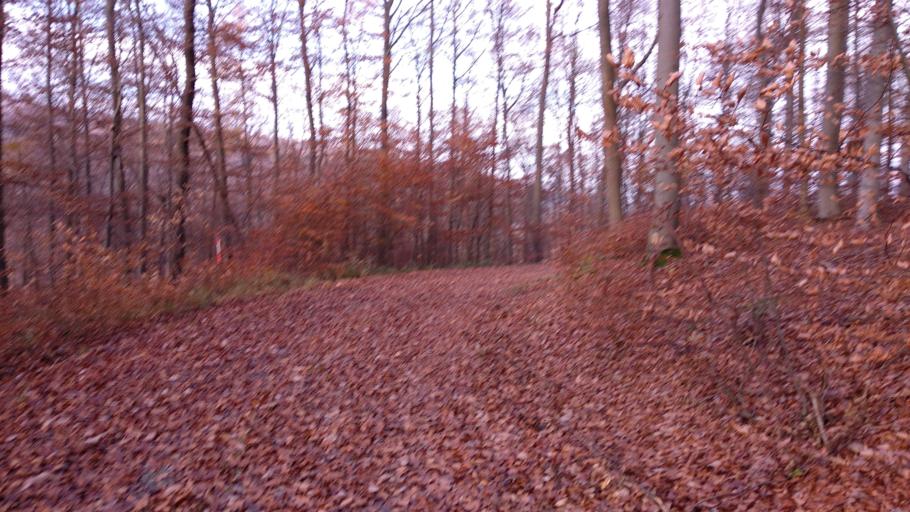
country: DE
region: North Rhine-Westphalia
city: Beverungen
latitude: 51.6594
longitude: 9.3206
